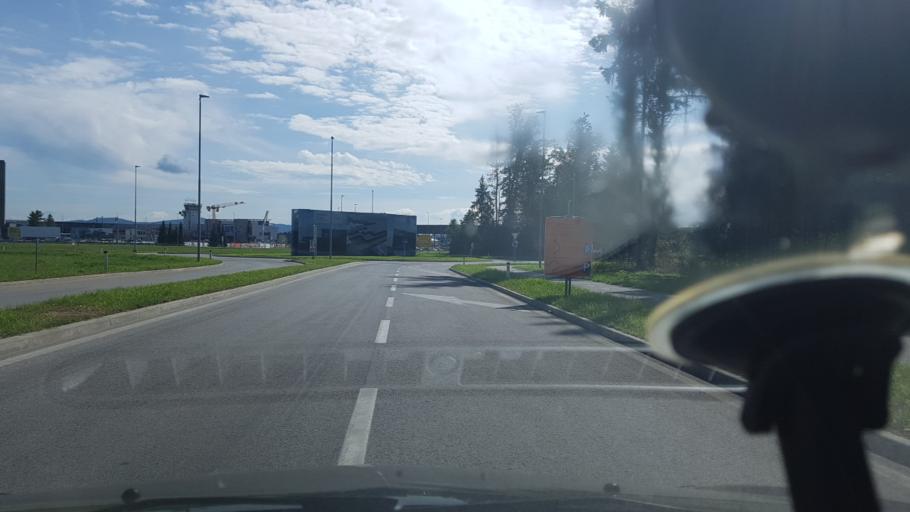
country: SI
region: Sencur
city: Sencur
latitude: 46.2351
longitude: 14.4515
